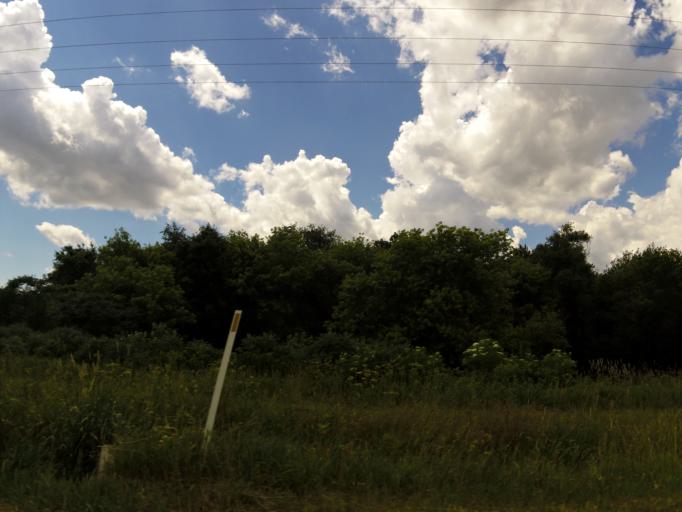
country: US
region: Iowa
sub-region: Fayette County
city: Oelwein
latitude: 42.5824
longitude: -91.9049
